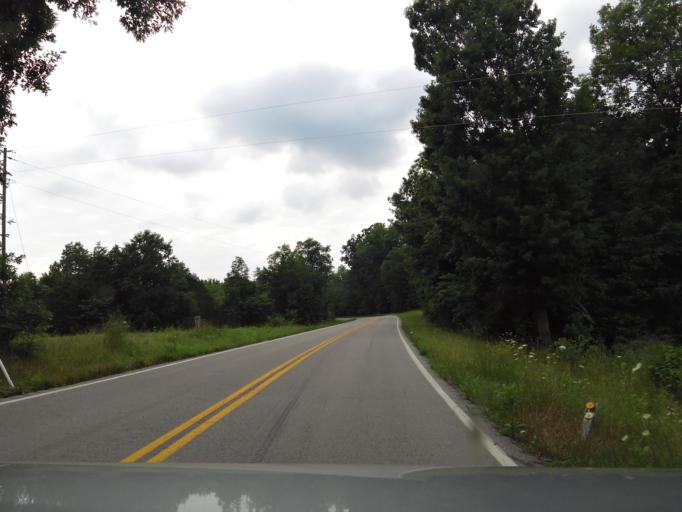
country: US
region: Kentucky
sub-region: Robertson County
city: Mount Olivet
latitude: 38.4995
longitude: -84.1002
